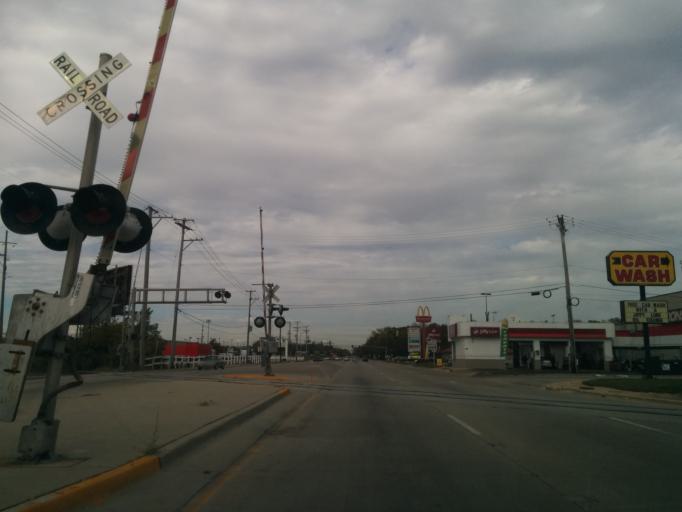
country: US
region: Illinois
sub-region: Cook County
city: River Grove
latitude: 41.9060
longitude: -87.8349
